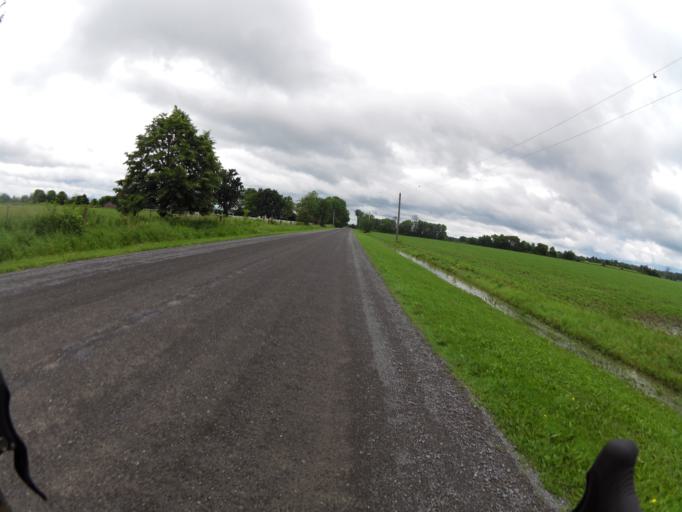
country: CA
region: Ontario
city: Bells Corners
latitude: 45.2570
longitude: -75.8608
